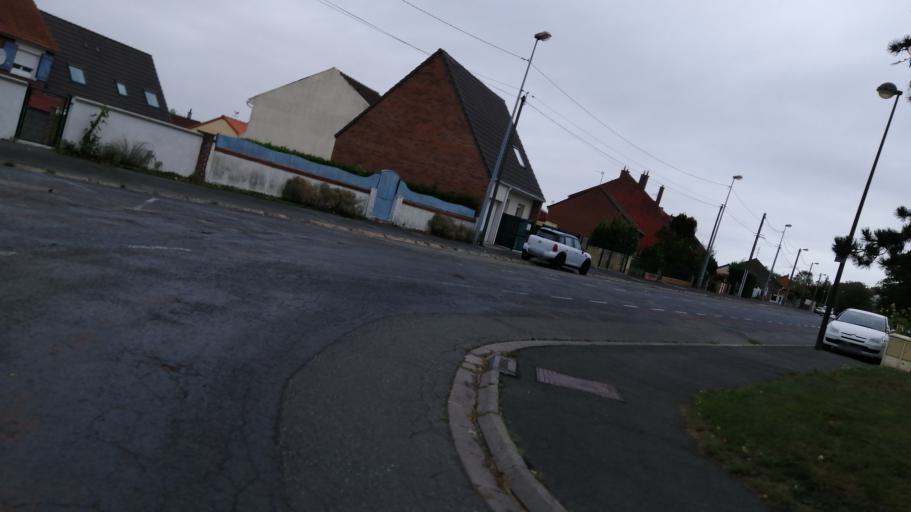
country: FR
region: Nord-Pas-de-Calais
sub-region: Departement du Pas-de-Calais
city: Anzin-Saint-Aubin
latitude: 50.2958
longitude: 2.7479
